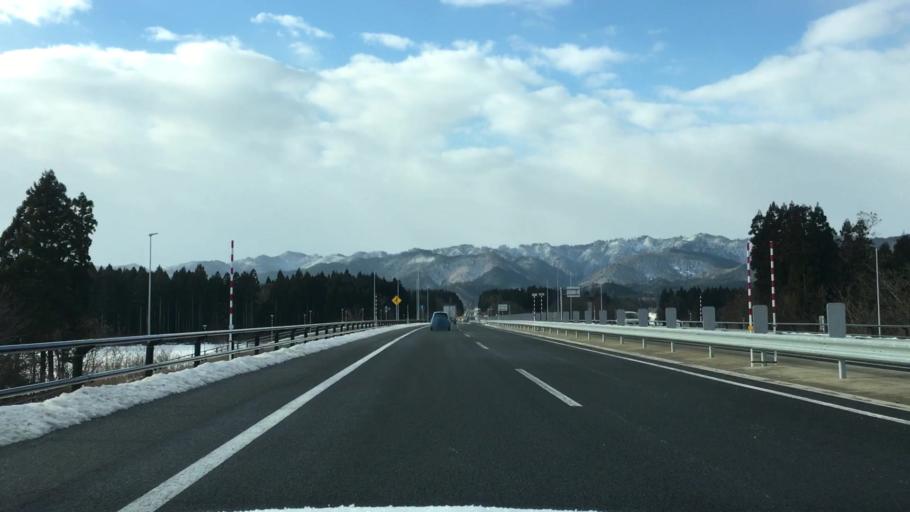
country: JP
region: Akita
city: Odate
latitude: 40.2500
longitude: 140.5158
